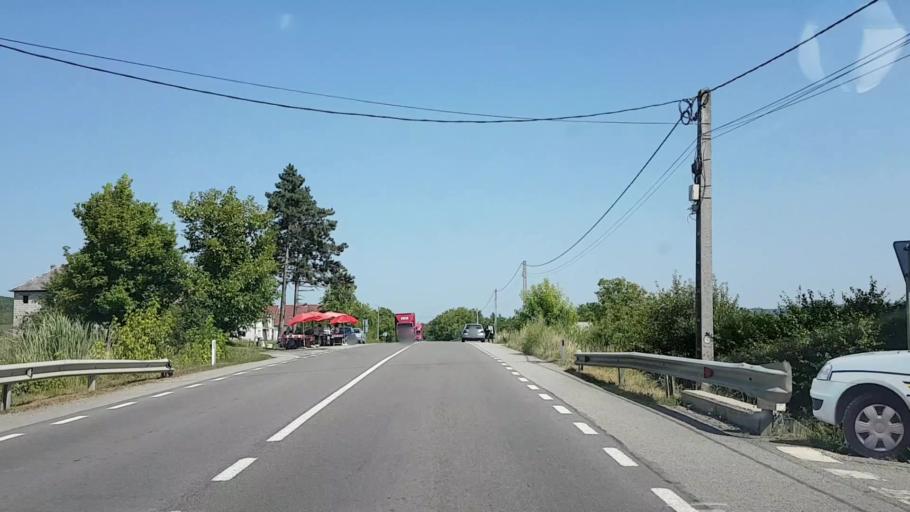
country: RO
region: Bistrita-Nasaud
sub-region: Comuna Uriu
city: Cristestii Ciceului
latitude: 47.1844
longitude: 24.1273
